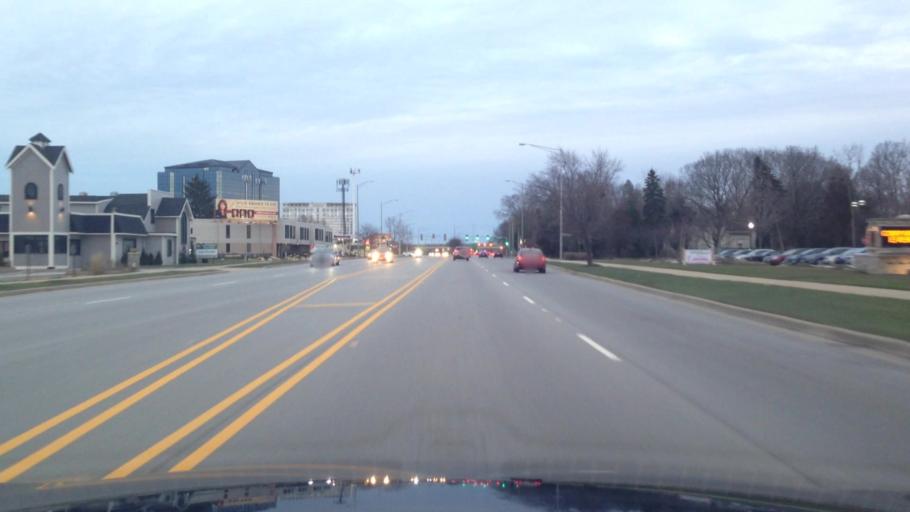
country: US
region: Illinois
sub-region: Cook County
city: Wheeling
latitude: 42.1587
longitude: -87.9179
